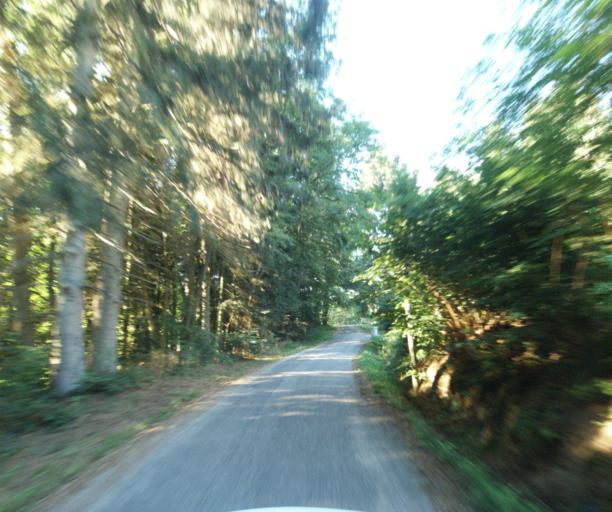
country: FR
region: Lorraine
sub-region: Departement des Vosges
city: Chantraine
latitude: 48.1429
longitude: 6.4635
